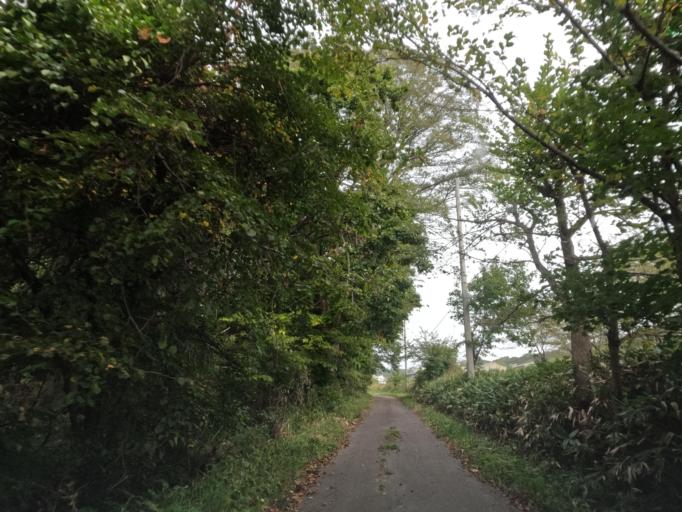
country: JP
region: Hokkaido
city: Date
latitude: 42.4120
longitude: 140.9271
